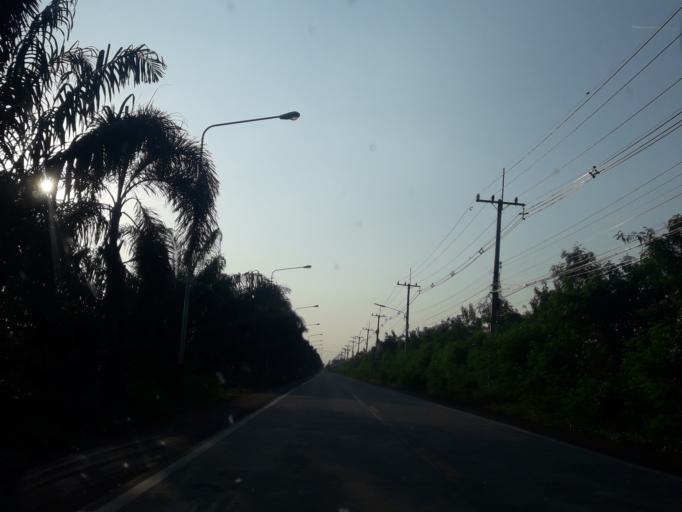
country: TH
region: Pathum Thani
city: Nong Suea
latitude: 14.1365
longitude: 100.8547
